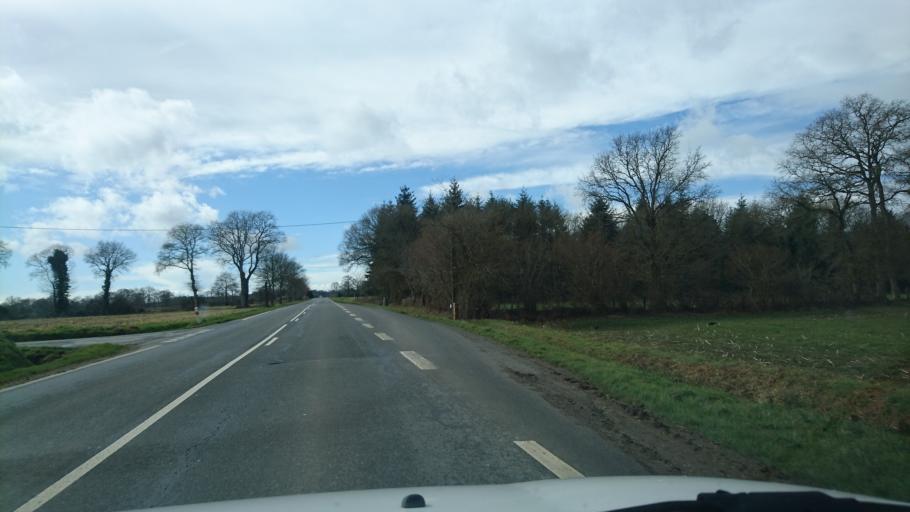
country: FR
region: Brittany
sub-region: Departement d'Ille-et-Vilaine
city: Sens-de-Bretagne
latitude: 48.3056
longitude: -1.5447
